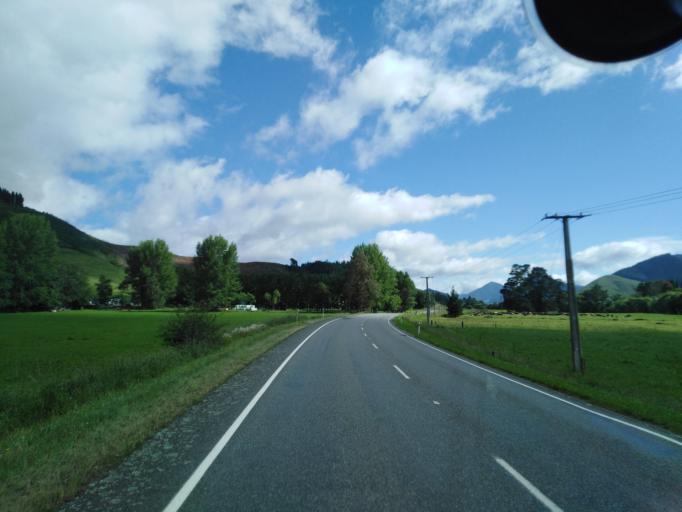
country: NZ
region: Nelson
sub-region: Nelson City
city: Nelson
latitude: -41.2681
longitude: 173.5725
